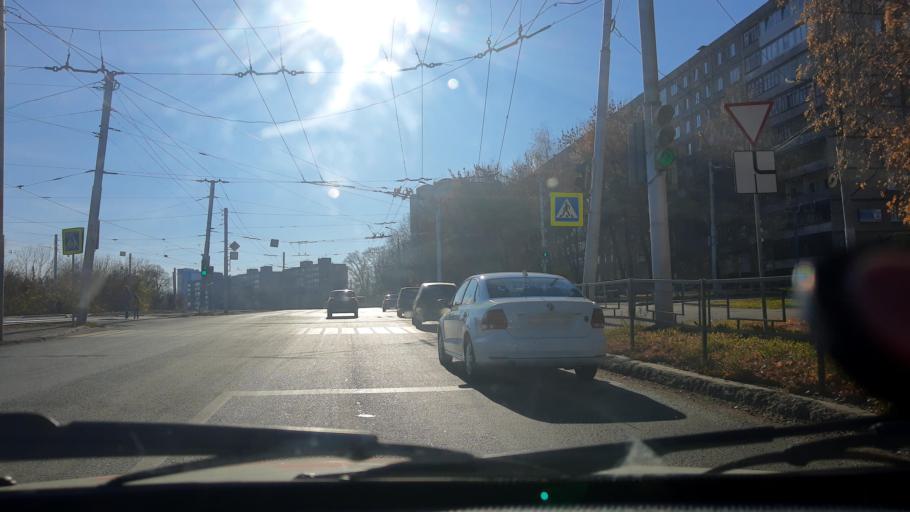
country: RU
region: Bashkortostan
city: Ufa
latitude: 54.8065
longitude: 56.1319
